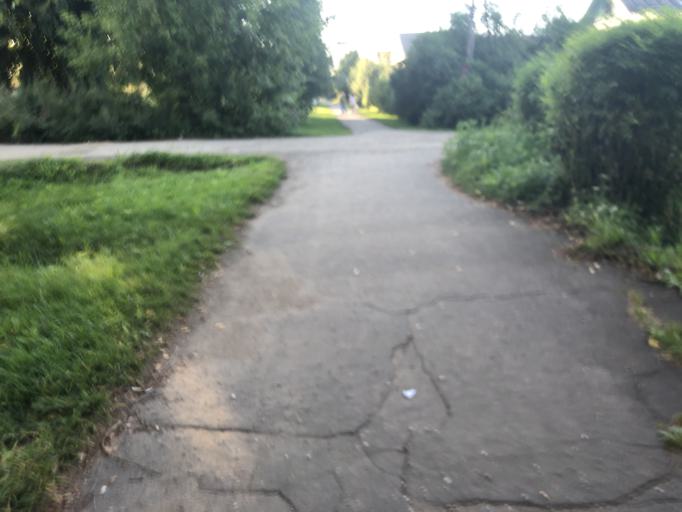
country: RU
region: Tverskaya
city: Rzhev
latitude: 56.2418
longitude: 34.3176
